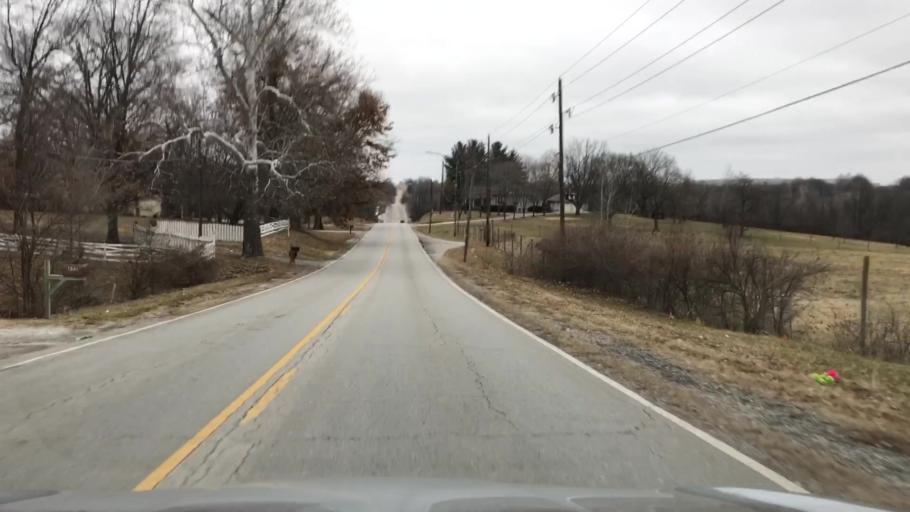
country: US
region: Missouri
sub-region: Clay County
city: Liberty
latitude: 39.2541
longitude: -94.4167
